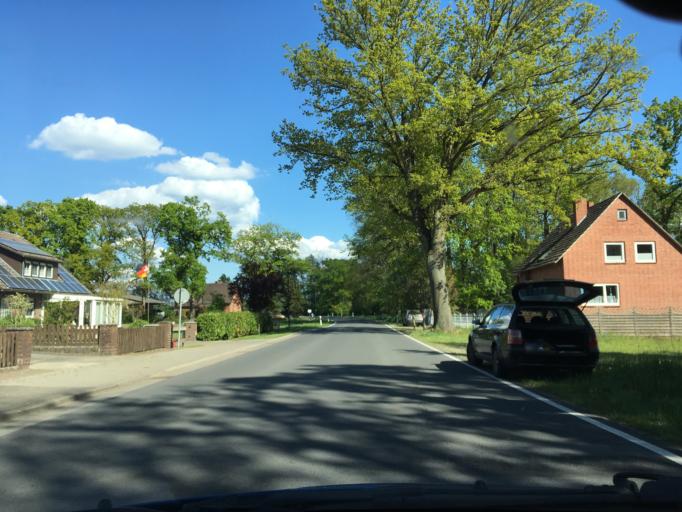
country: DE
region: Brandenburg
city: Lanz
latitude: 53.0157
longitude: 11.5453
